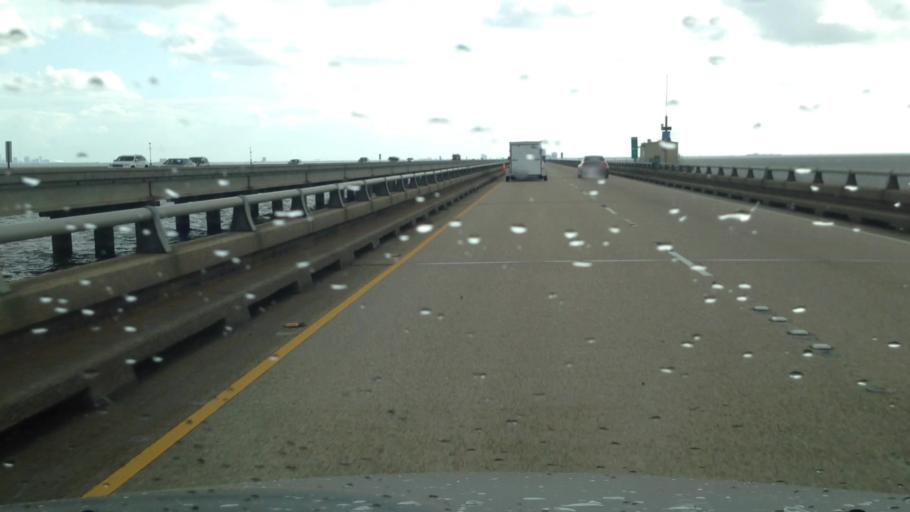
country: US
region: Louisiana
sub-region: Jefferson Parish
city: Metairie
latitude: 30.1099
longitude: -90.1387
